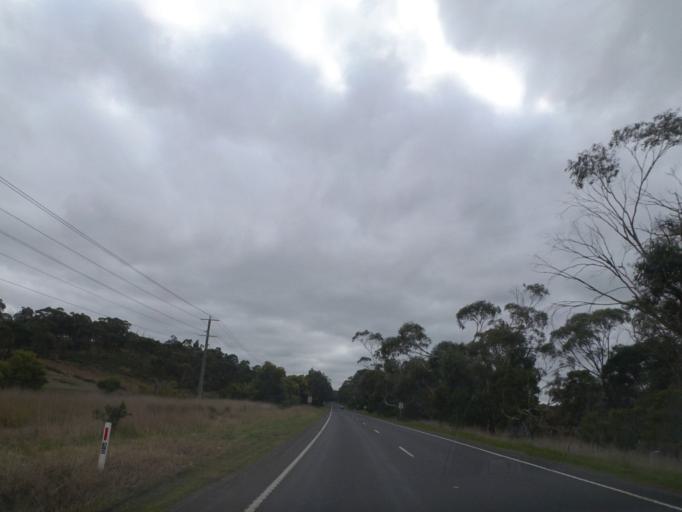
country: AU
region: Victoria
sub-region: Whittlesea
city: Whittlesea
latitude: -37.3929
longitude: 145.0278
